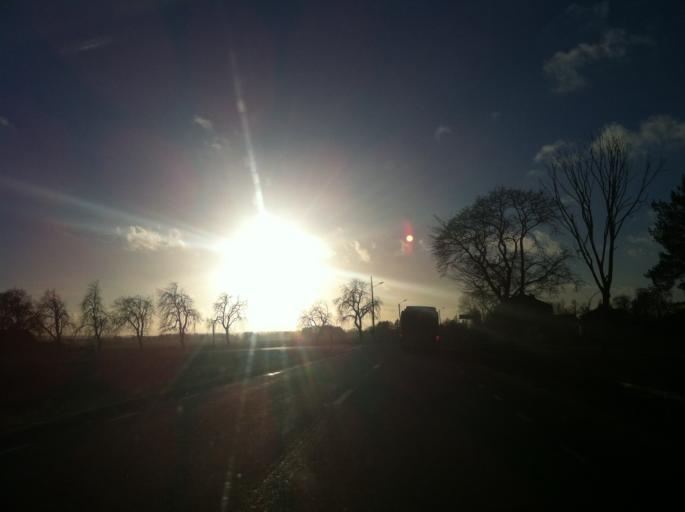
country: SE
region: Skane
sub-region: Hassleholms Kommun
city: Hastveda
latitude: 56.1962
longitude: 13.9315
